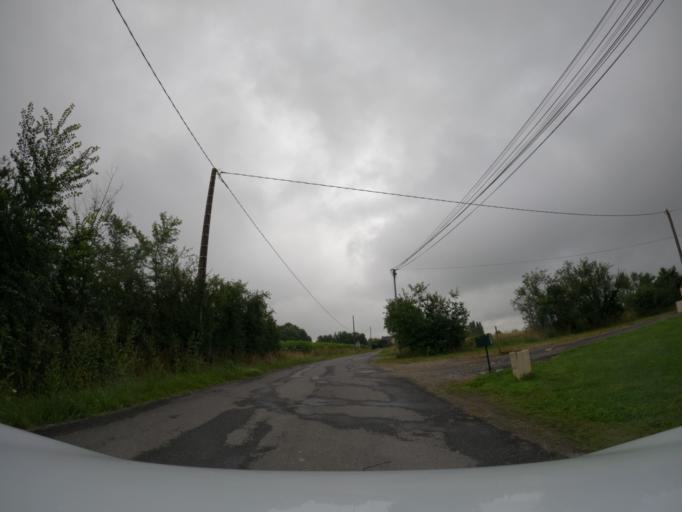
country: FR
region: Pays de la Loire
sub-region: Departement de la Loire-Atlantique
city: Saint-Mars-du-Desert
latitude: 47.3825
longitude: -1.4117
